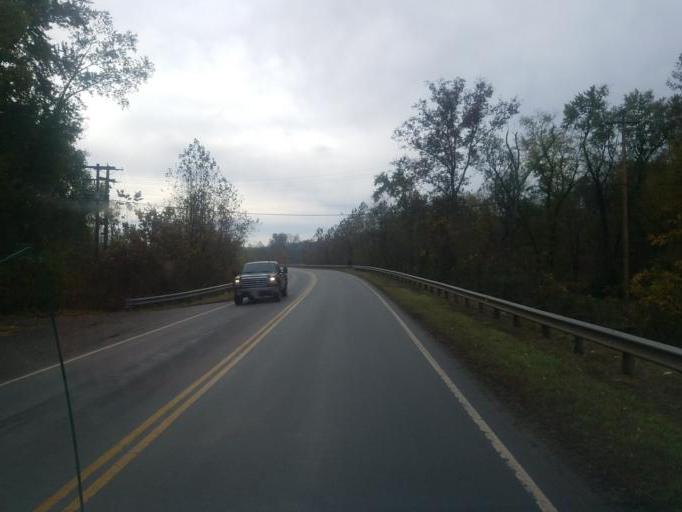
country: US
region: Ohio
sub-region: Washington County
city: Beverly
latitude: 39.5499
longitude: -81.6483
